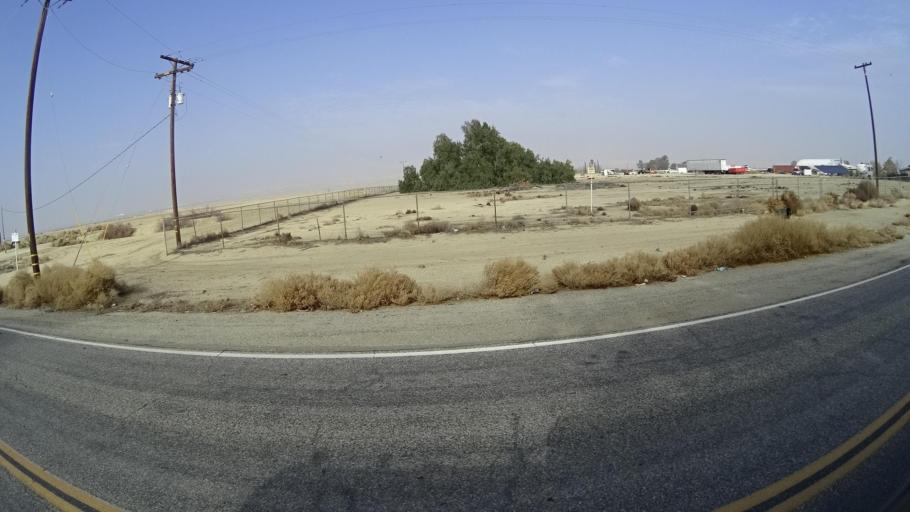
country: US
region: California
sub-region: Kern County
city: Ford City
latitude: 35.2097
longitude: -119.4113
